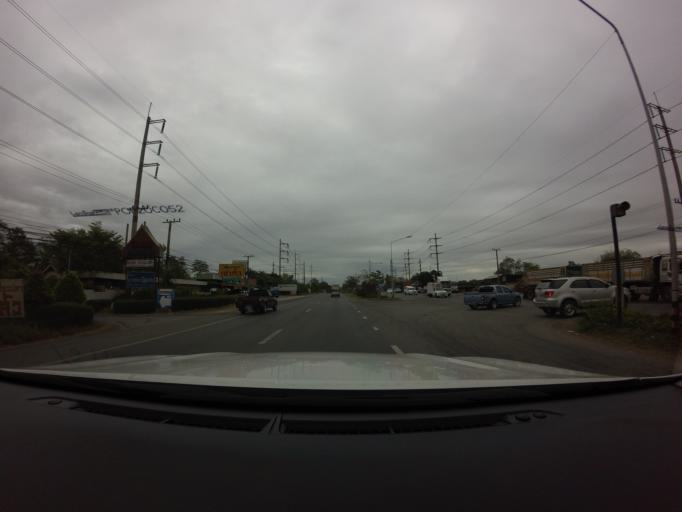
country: TH
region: Chachoengsao
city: Chachoengsao
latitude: 13.6593
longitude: 101.0580
